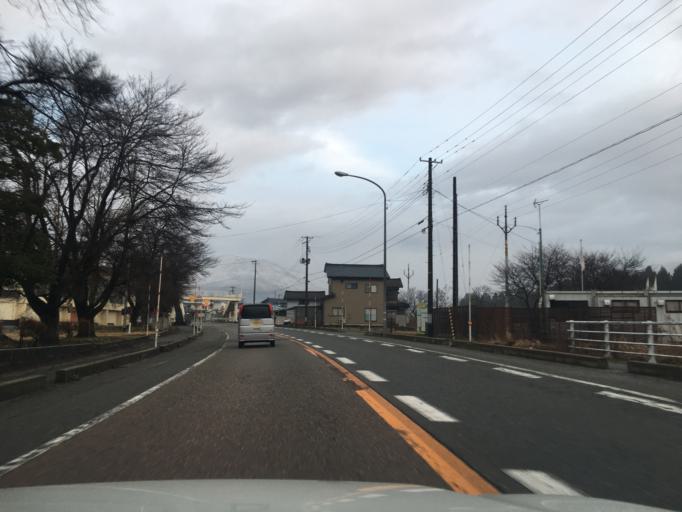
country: JP
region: Niigata
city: Murakami
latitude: 38.3323
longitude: 139.5552
